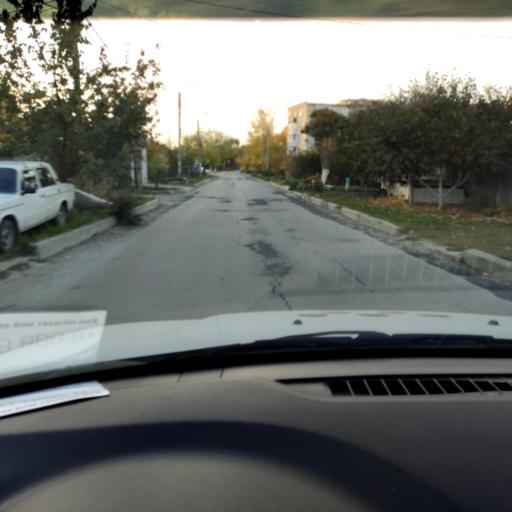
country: RU
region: Samara
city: Tol'yatti
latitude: 53.5312
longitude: 49.4022
